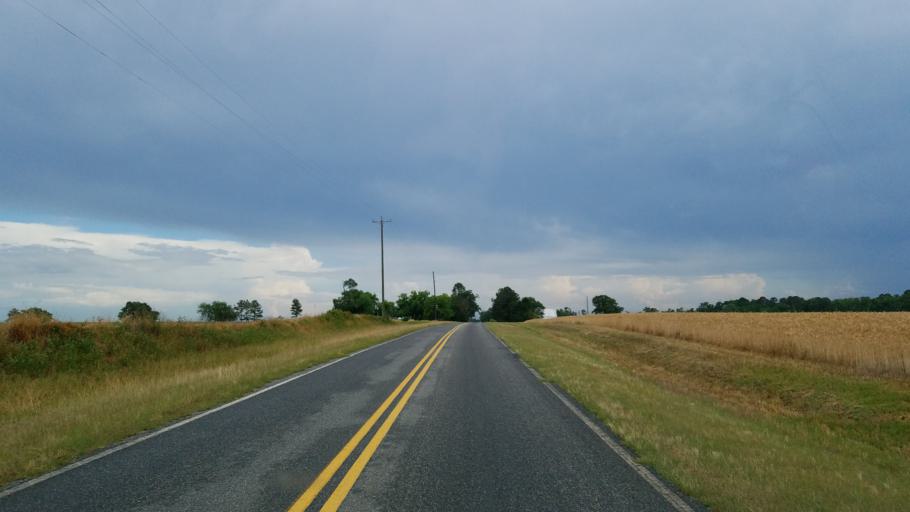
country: US
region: Georgia
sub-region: Dooly County
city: Unadilla
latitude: 32.1943
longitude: -83.7972
